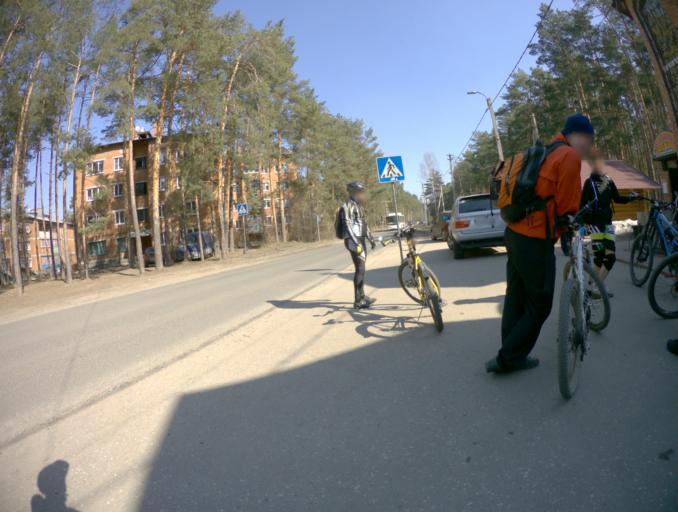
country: RU
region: Vladimir
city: Kommunar
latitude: 56.1204
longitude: 40.4612
